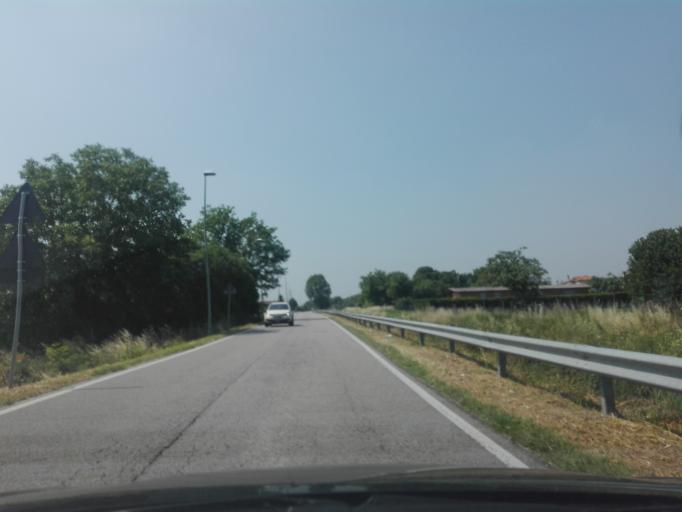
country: IT
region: Veneto
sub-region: Provincia di Rovigo
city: Ceregnano
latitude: 45.0660
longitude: 11.8724
